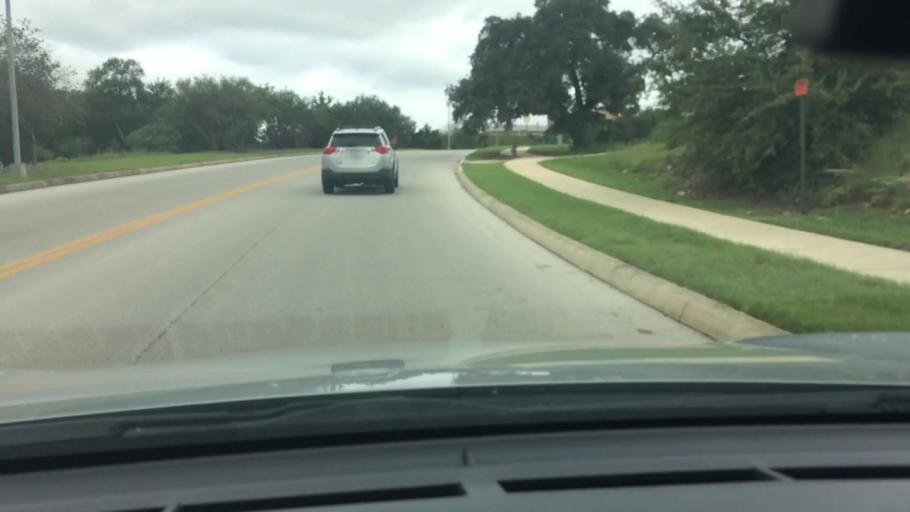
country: US
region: Texas
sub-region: Bexar County
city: Timberwood Park
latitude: 29.6590
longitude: -98.4010
